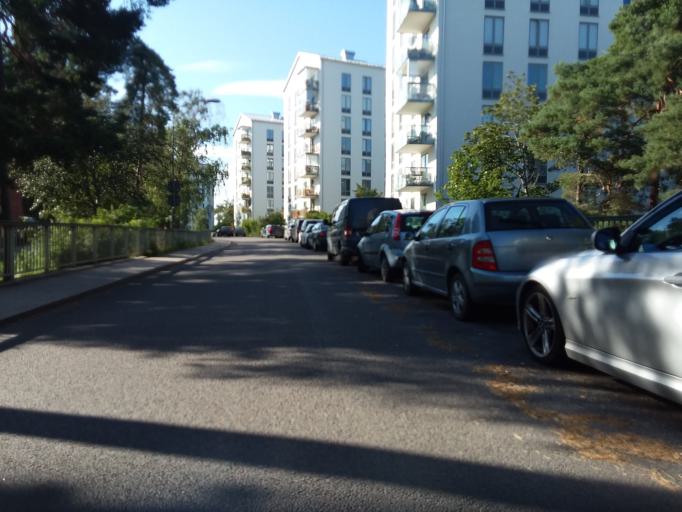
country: SE
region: Stockholm
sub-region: Stockholms Kommun
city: Bromma
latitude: 59.3458
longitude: 17.8792
